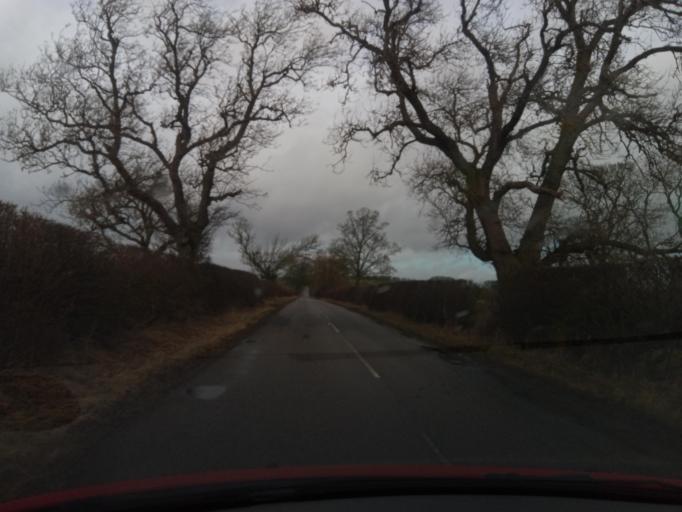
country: GB
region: England
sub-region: Northumberland
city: Rothley
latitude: 55.1811
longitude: -1.9683
